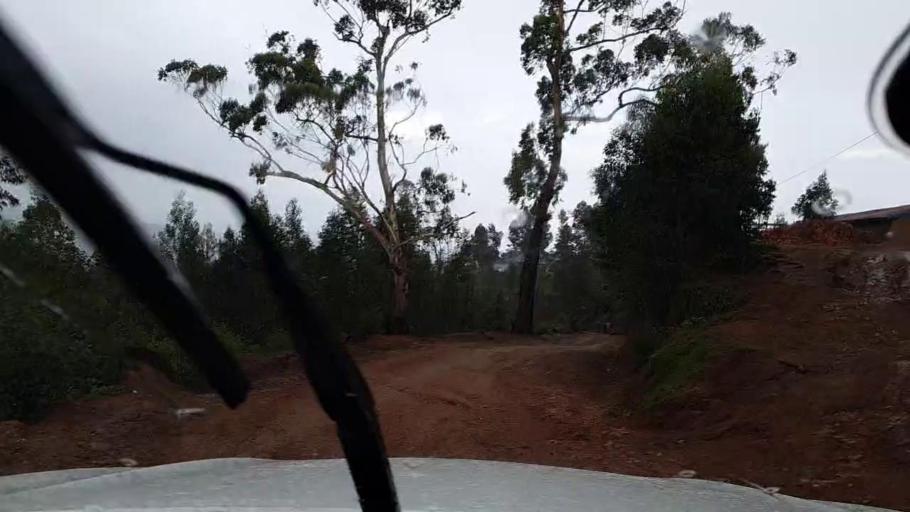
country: BI
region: Kayanza
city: Kayanza
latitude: -2.7848
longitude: 29.5322
